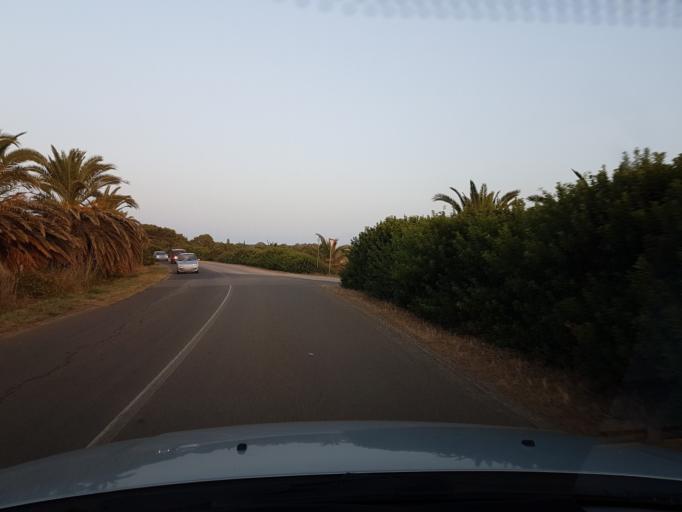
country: IT
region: Sardinia
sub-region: Provincia di Oristano
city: Cabras
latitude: 39.9501
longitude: 8.4112
